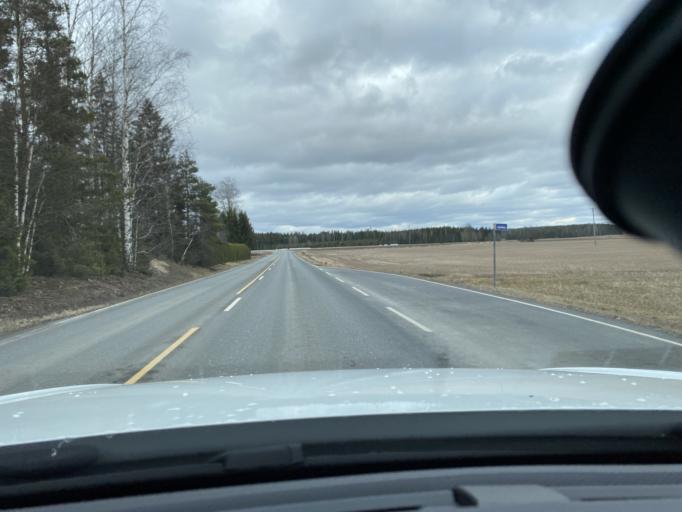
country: FI
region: Pirkanmaa
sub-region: Lounais-Pirkanmaa
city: Punkalaidun
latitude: 61.1040
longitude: 23.1654
